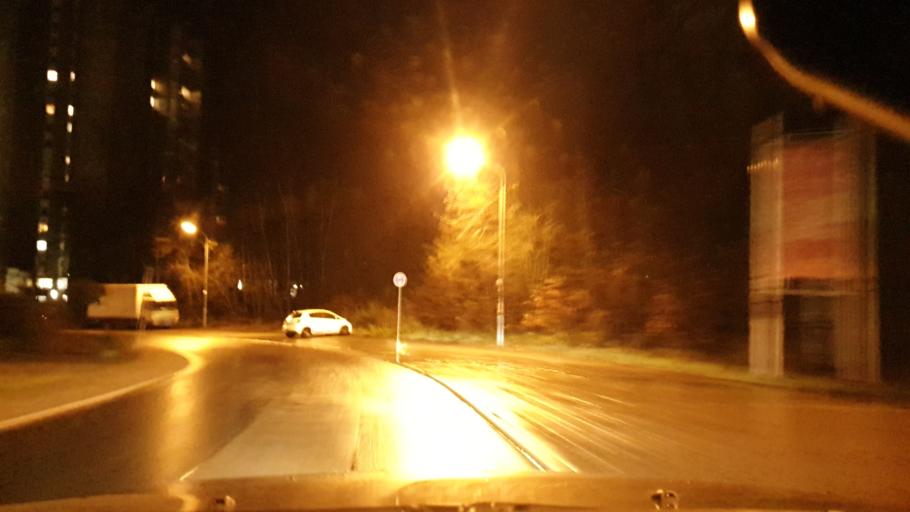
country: DE
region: Rheinland-Pfalz
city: Kaiserslautern
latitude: 49.4330
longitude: 7.7794
